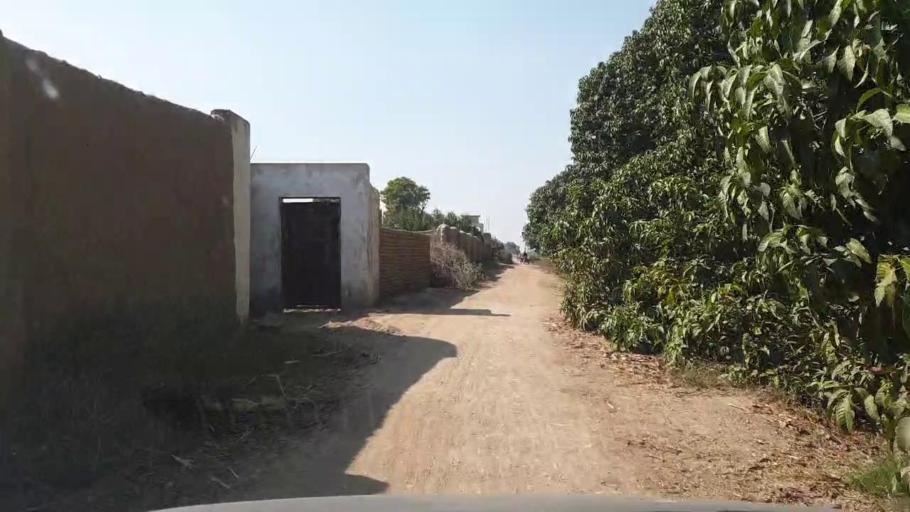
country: PK
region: Sindh
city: Tando Jam
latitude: 25.4034
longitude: 68.6307
